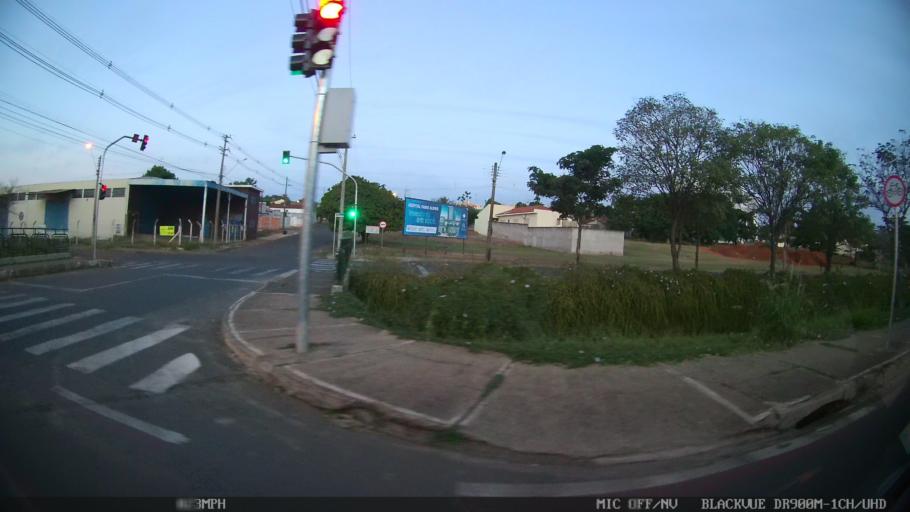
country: BR
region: Sao Paulo
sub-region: Catanduva
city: Catanduva
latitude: -21.1313
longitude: -48.9858
